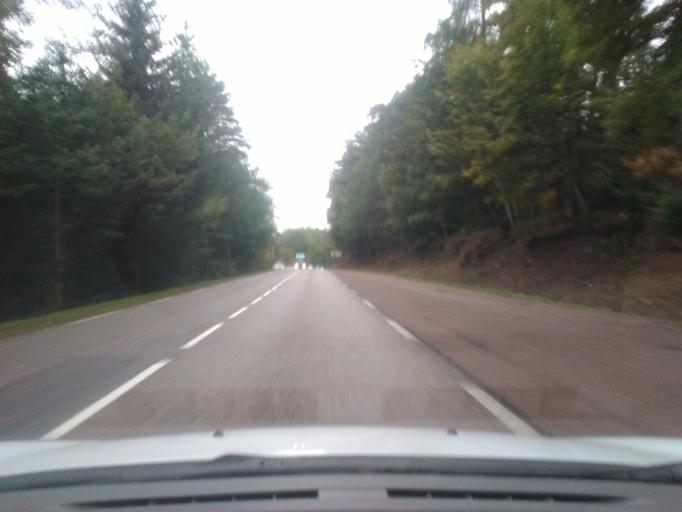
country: FR
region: Lorraine
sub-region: Departement des Vosges
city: Jeanmenil
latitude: 48.3237
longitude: 6.7400
